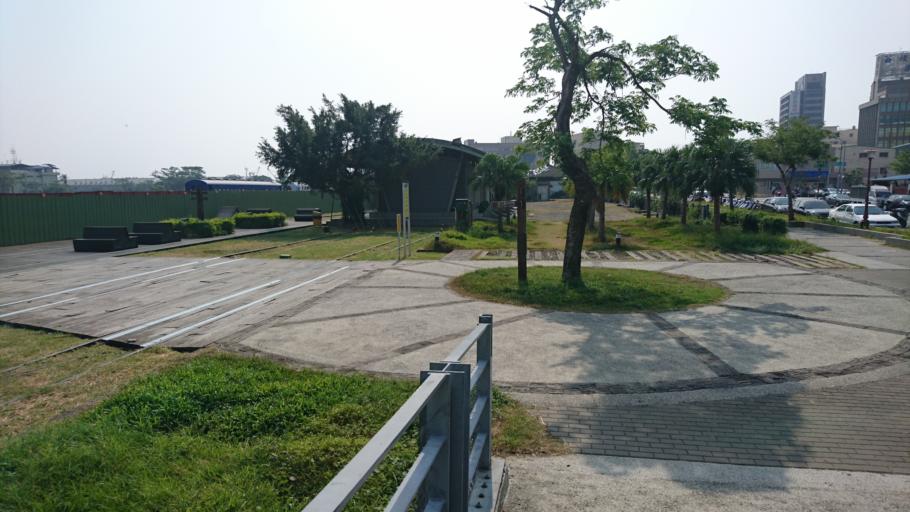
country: TW
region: Kaohsiung
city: Kaohsiung
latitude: 22.6227
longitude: 120.2760
